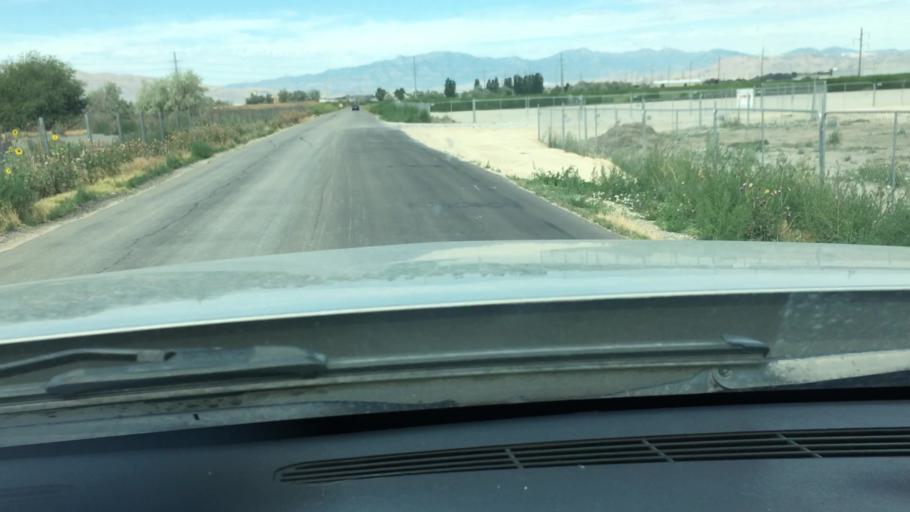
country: US
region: Utah
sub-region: Utah County
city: Pleasant Grove
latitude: 40.3442
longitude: -111.7677
